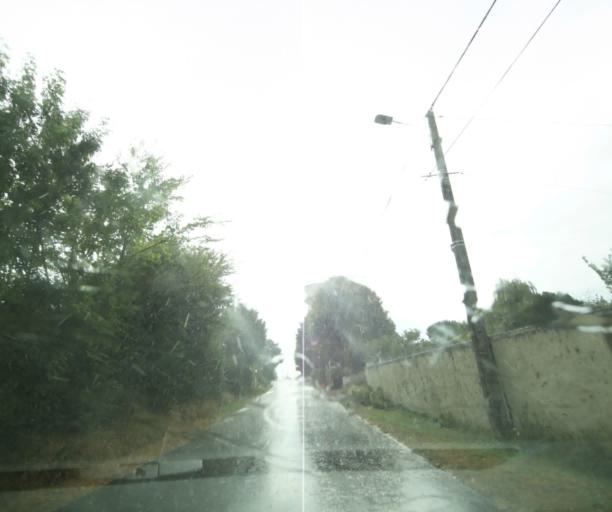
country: FR
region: Poitou-Charentes
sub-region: Departement de la Charente-Maritime
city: Tonnay-Charente
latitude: 45.9505
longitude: -0.8756
